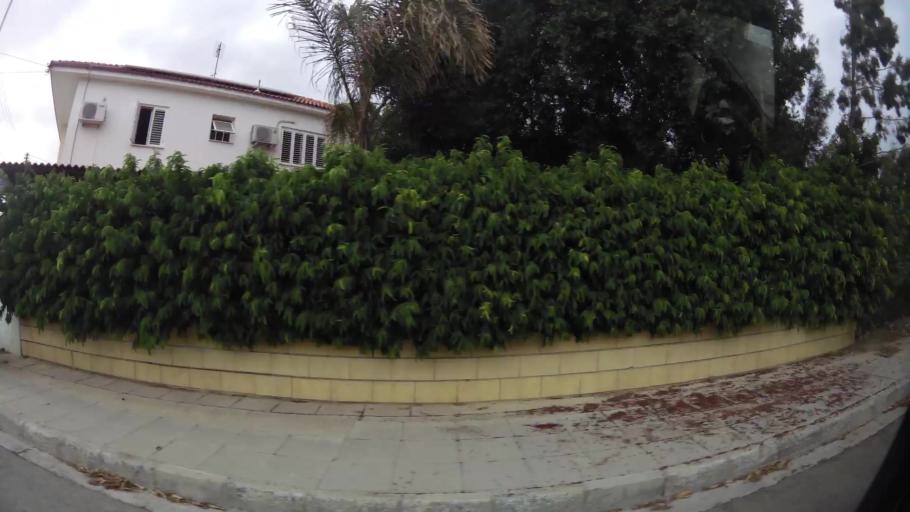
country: CY
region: Lefkosia
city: Geri
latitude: 35.1000
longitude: 33.3894
